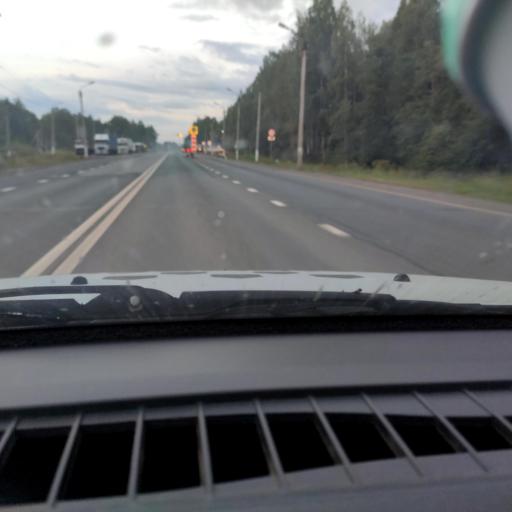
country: RU
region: Kirov
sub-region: Kirovo-Chepetskiy Rayon
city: Kirov
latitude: 58.6814
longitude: 49.6439
